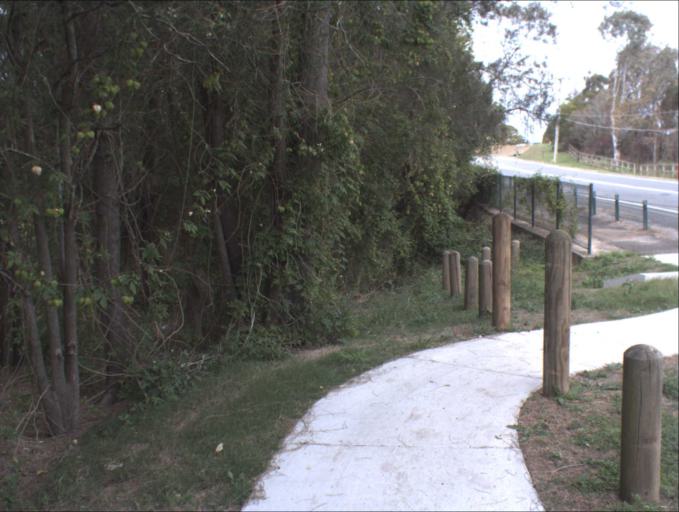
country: AU
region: Queensland
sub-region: Logan
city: Waterford West
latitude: -27.6980
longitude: 153.1181
